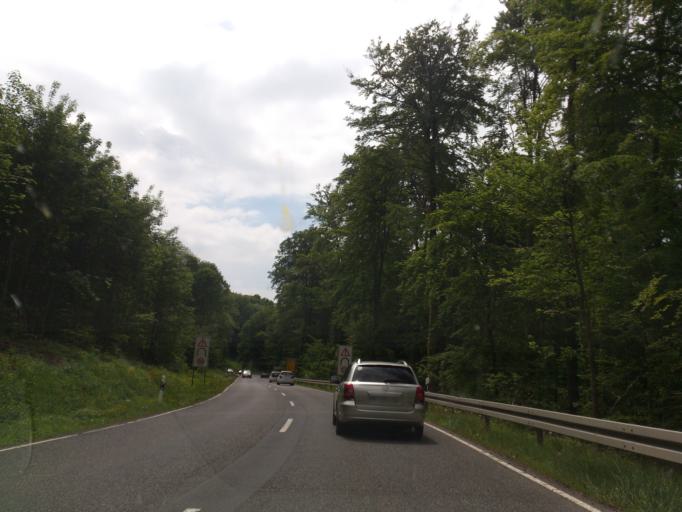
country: DE
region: Hesse
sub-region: Regierungsbezirk Kassel
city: Calden
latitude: 51.3465
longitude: 9.3811
